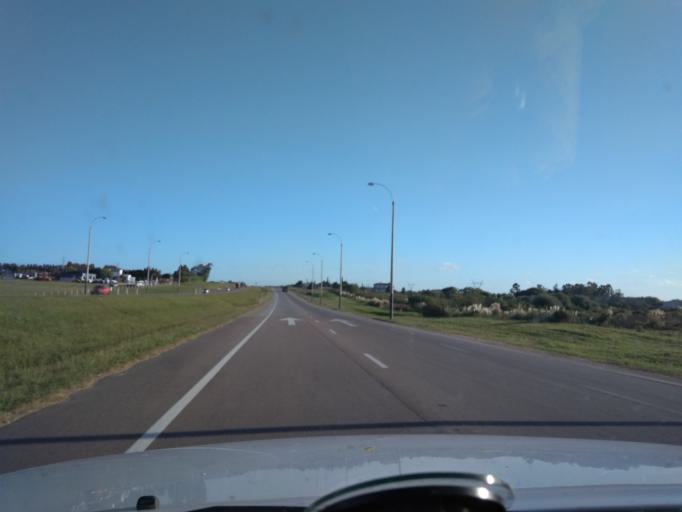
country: UY
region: Canelones
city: Las Piedras
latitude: -34.7263
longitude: -56.2477
